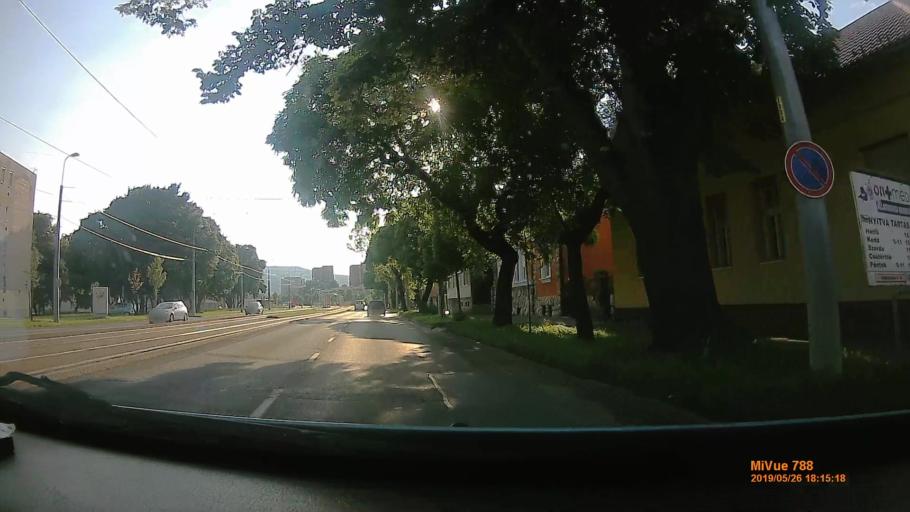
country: HU
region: Borsod-Abauj-Zemplen
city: Miskolc
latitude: 48.1009
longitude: 20.7212
